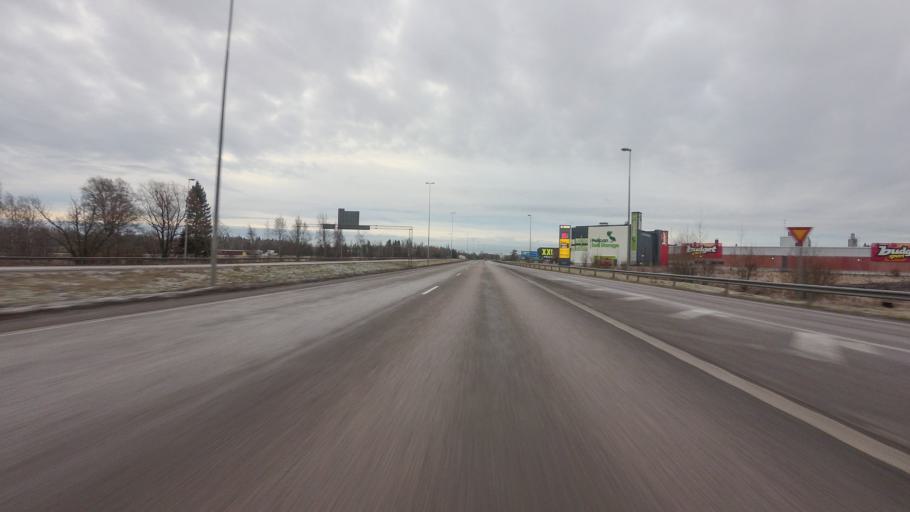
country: FI
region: Uusimaa
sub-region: Helsinki
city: Vantaa
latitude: 60.2802
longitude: 24.9778
